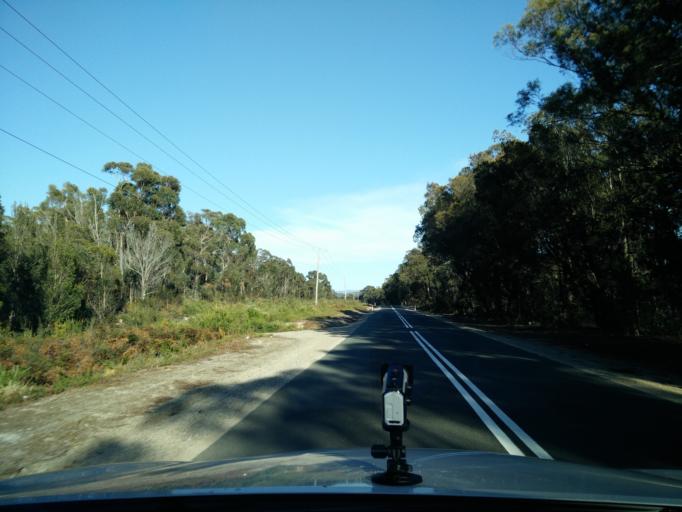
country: AU
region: Tasmania
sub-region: Break O'Day
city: St Helens
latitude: -41.2930
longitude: 148.1822
